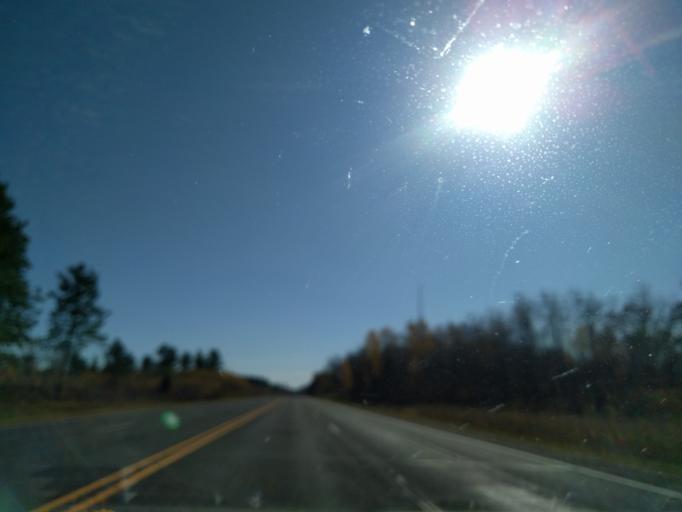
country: US
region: Michigan
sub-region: Iron County
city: Crystal Falls
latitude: 46.2284
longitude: -88.0075
